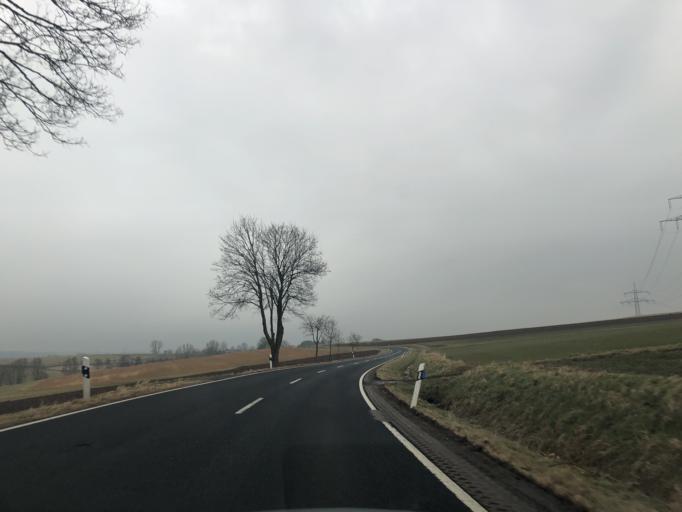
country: DE
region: Hesse
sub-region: Regierungsbezirk Darmstadt
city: Birstein
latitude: 50.3731
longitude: 9.3009
